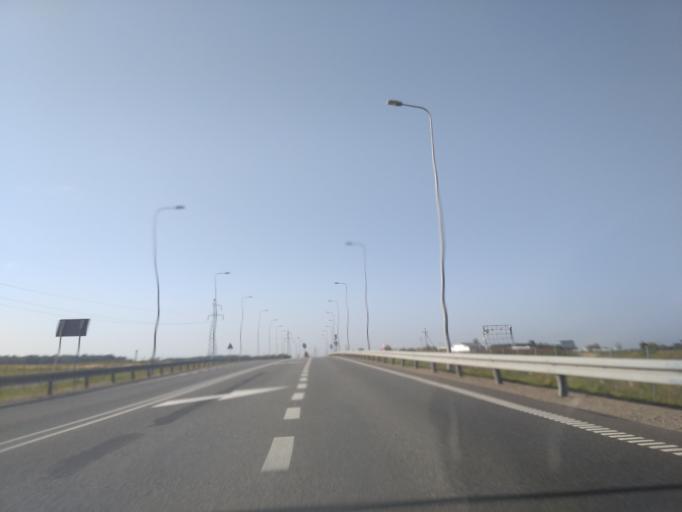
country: PL
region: Subcarpathian Voivodeship
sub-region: Powiat rzeszowski
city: Wolka Podlesna
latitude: 50.1688
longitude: 22.0874
